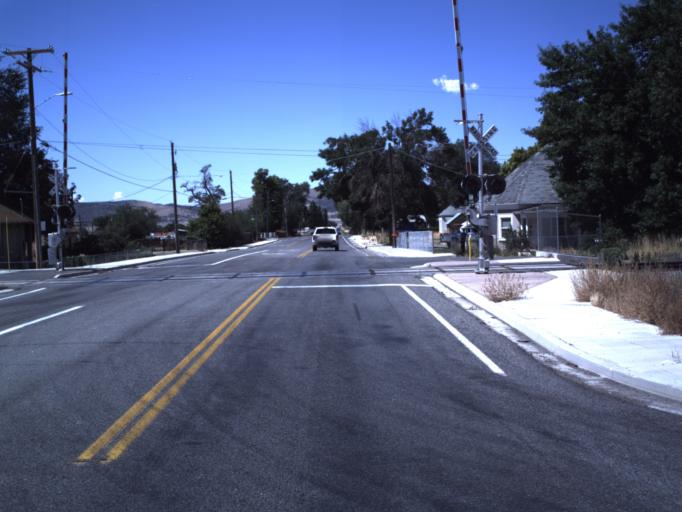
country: US
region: Utah
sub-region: Juab County
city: Nephi
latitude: 39.7100
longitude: -111.8415
